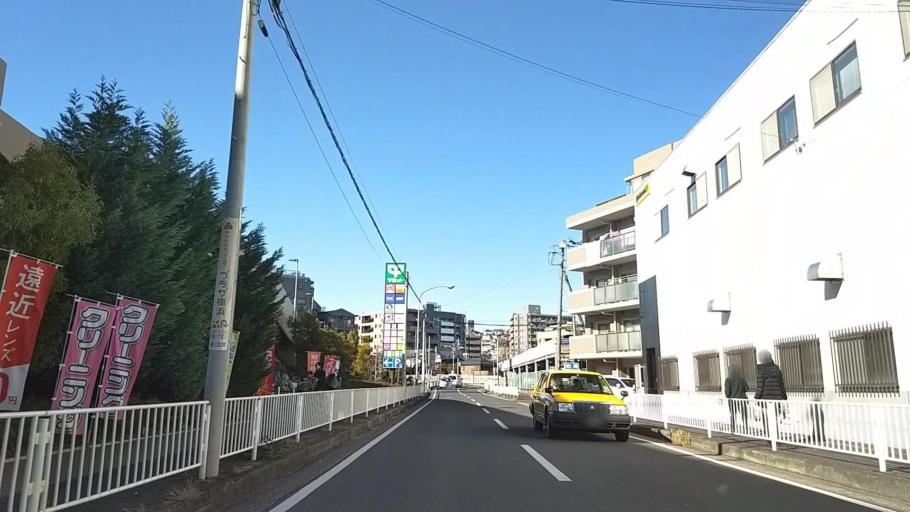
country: JP
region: Kanagawa
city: Yokohama
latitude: 35.4597
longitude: 139.6112
